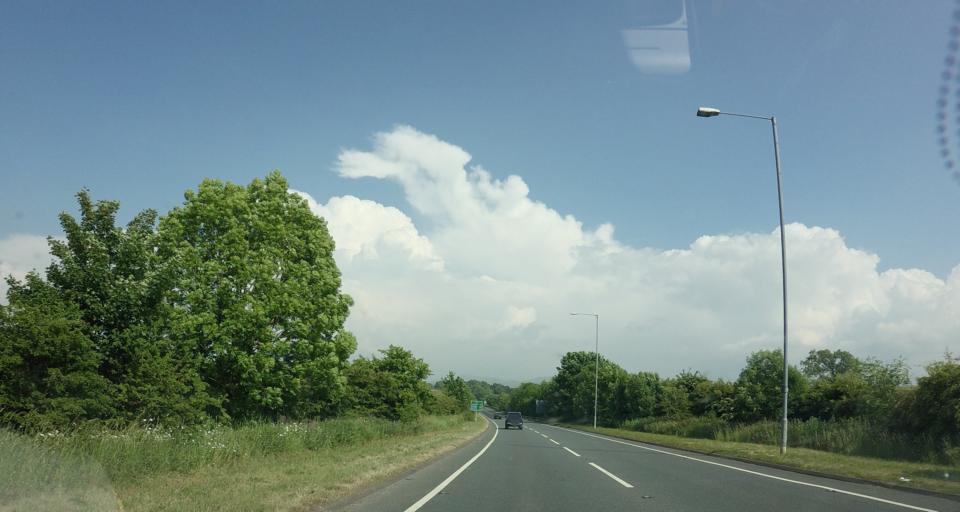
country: GB
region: England
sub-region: Cumbria
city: Cockermouth
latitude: 54.6525
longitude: -3.3704
